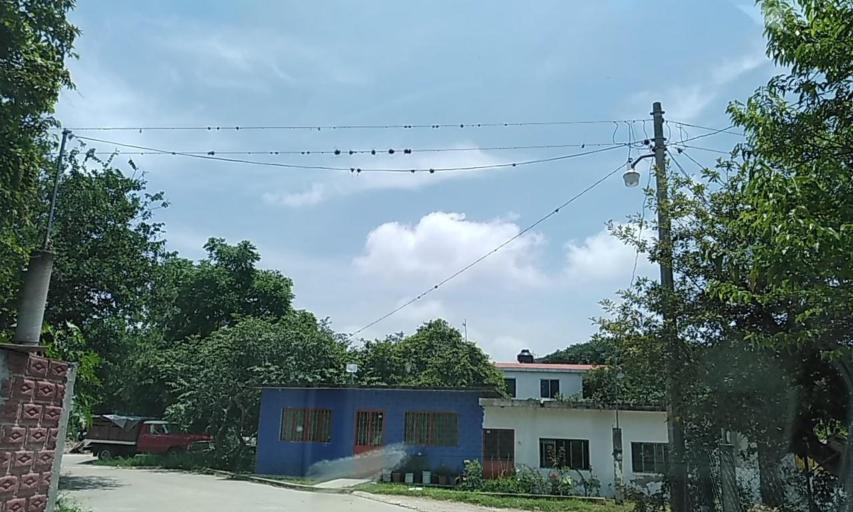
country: MX
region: Veracruz
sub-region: Emiliano Zapata
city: Dos Rios
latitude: 19.4394
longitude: -96.7523
